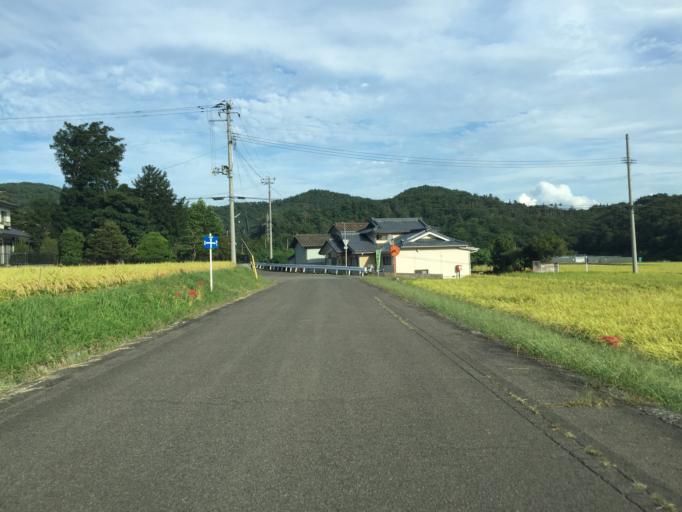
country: JP
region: Fukushima
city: Hobaramachi
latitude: 37.8889
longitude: 140.5307
